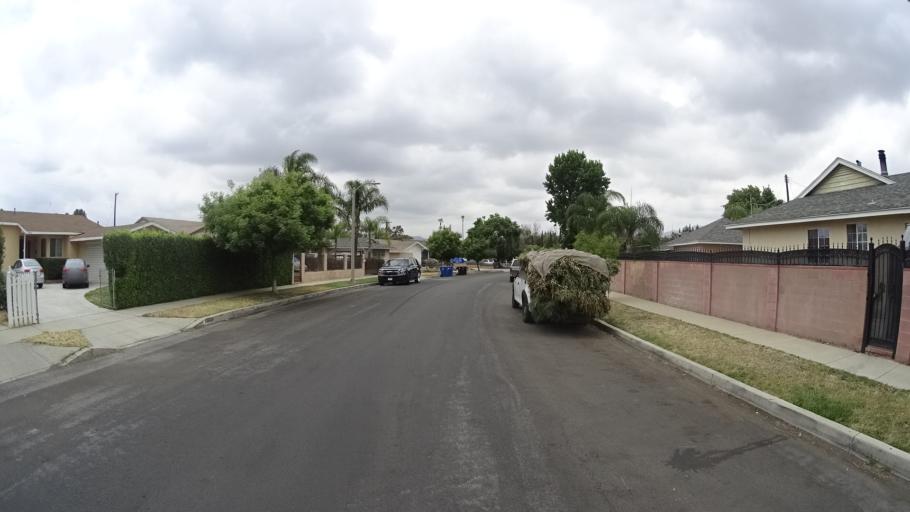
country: US
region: California
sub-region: Los Angeles County
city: San Fernando
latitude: 34.2639
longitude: -118.4477
